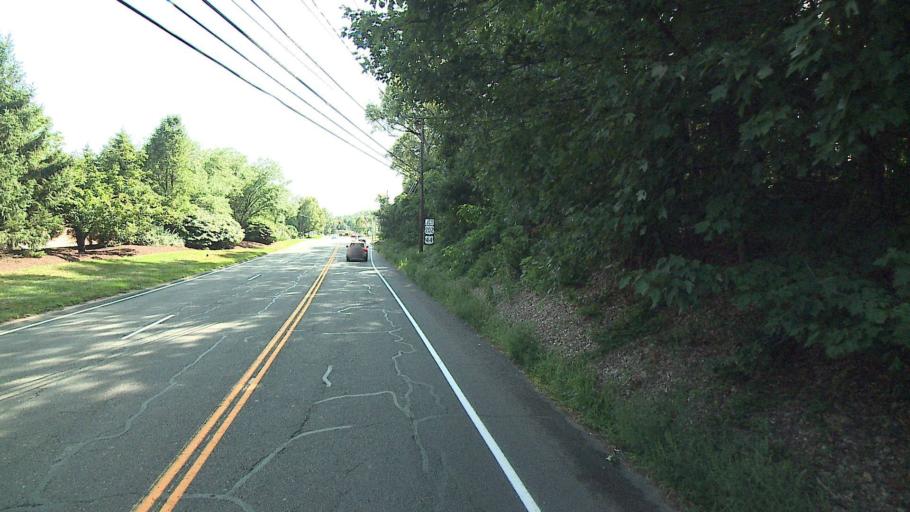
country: US
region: Connecticut
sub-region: Hartford County
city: Canton Valley
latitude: 41.8190
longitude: -72.8664
